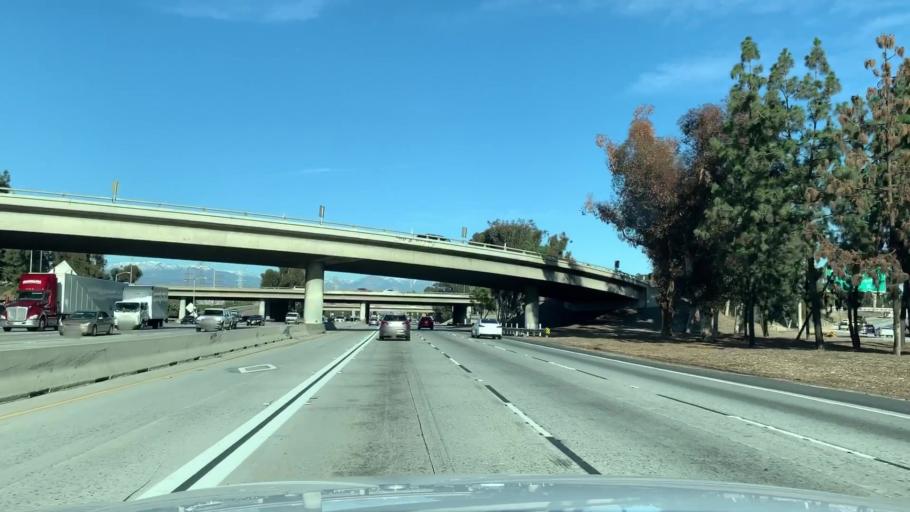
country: US
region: California
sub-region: Los Angeles County
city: South El Monte
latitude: 34.0326
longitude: -118.0289
